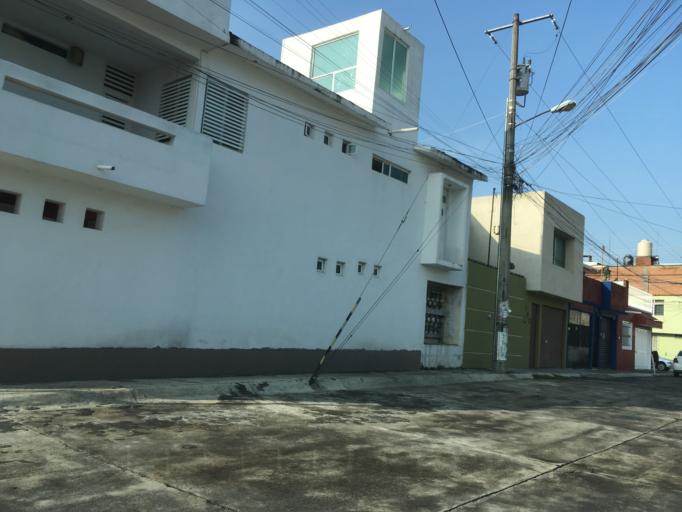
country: MX
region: Michoacan
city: Morelia
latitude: 19.6953
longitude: -101.2178
